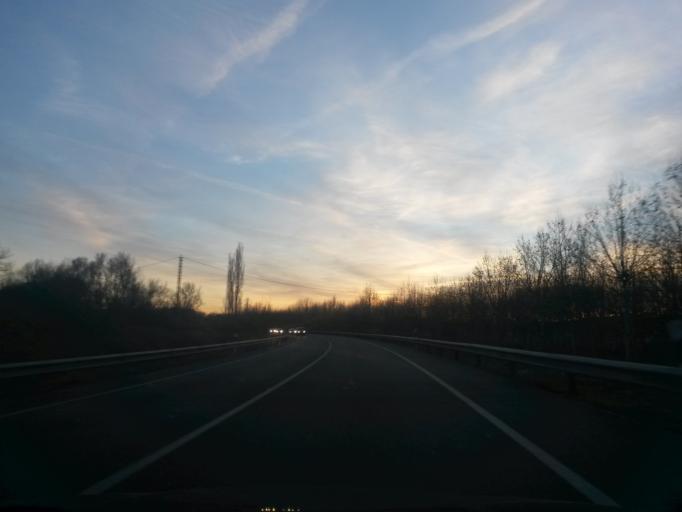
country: ES
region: Catalonia
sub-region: Provincia de Girona
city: Quart d'Onyar
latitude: 41.9485
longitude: 2.8273
